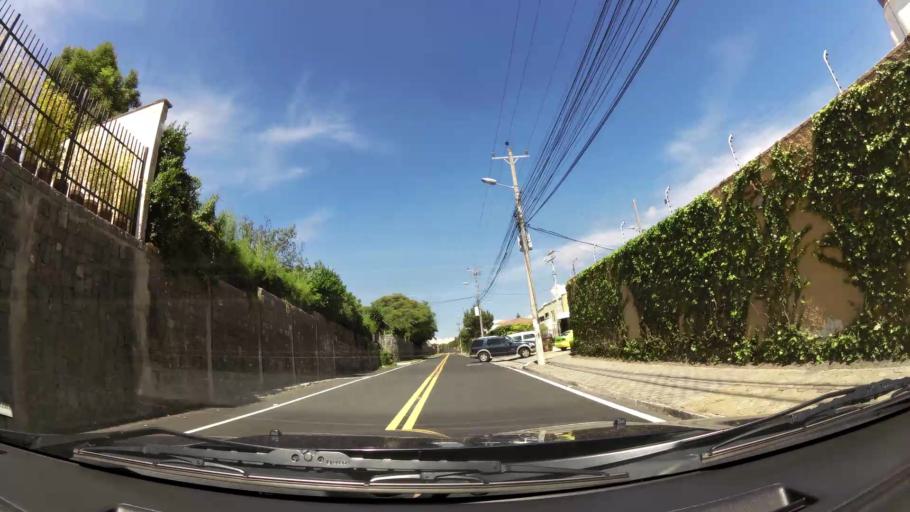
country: EC
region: Pichincha
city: Quito
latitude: -0.2080
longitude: -78.4352
